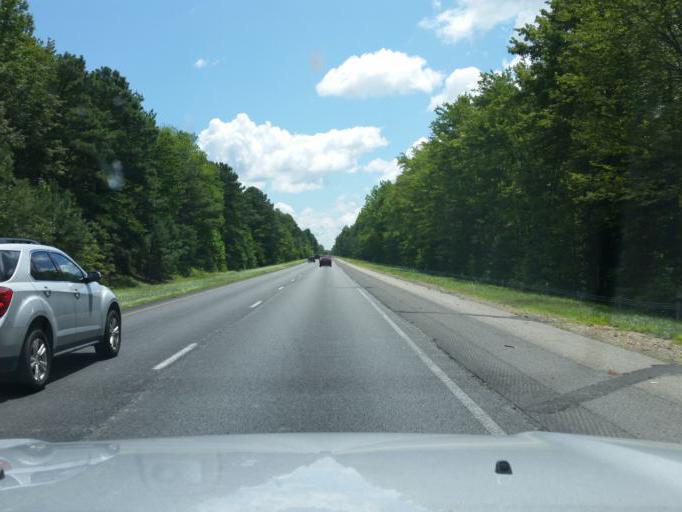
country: US
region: Virginia
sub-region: New Kent County
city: New Kent
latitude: 37.4914
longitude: -76.9953
